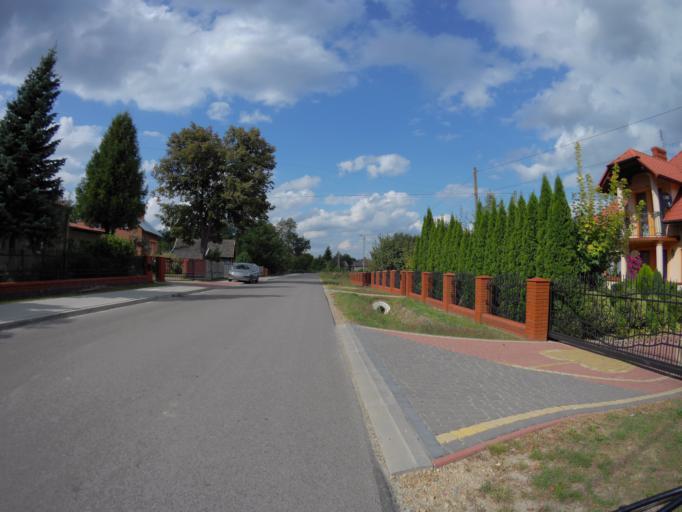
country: PL
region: Subcarpathian Voivodeship
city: Nowa Sarzyna
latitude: 50.2835
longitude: 22.3509
